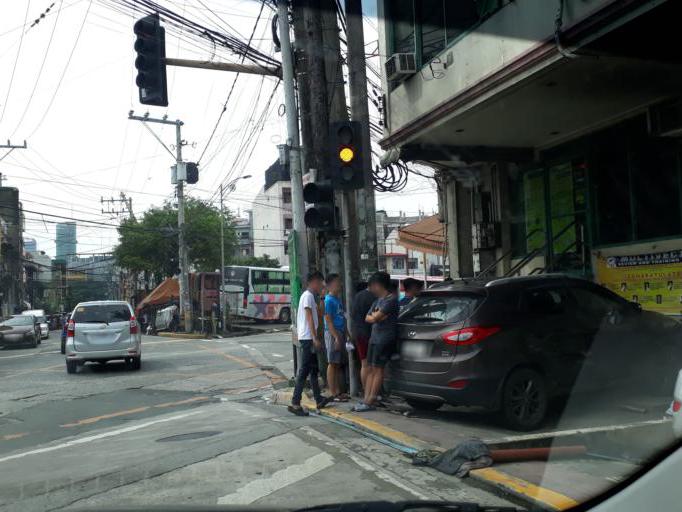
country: PH
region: Metro Manila
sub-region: City of Manila
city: Manila
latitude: 14.6069
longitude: 120.9934
